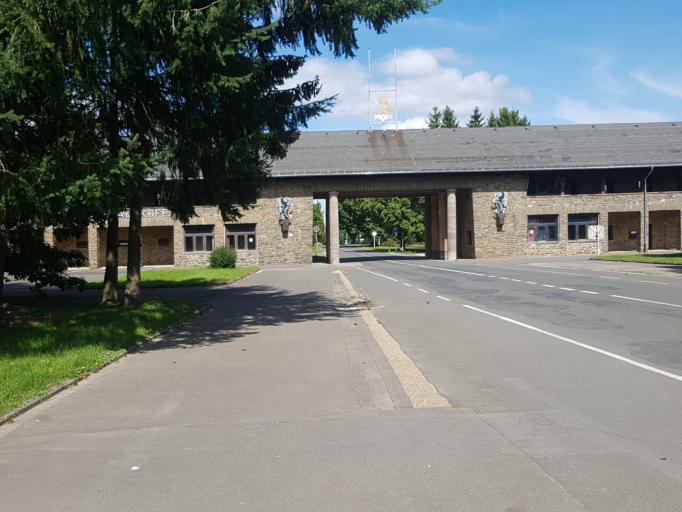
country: DE
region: North Rhine-Westphalia
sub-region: Regierungsbezirk Koln
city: Schleiden
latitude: 50.5800
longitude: 6.4470
